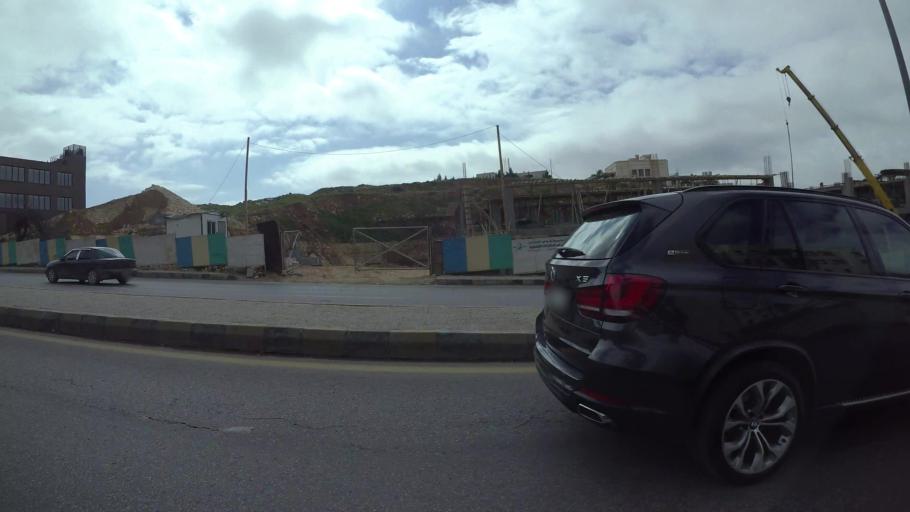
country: JO
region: Amman
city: Al Jubayhah
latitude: 31.9958
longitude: 35.8341
